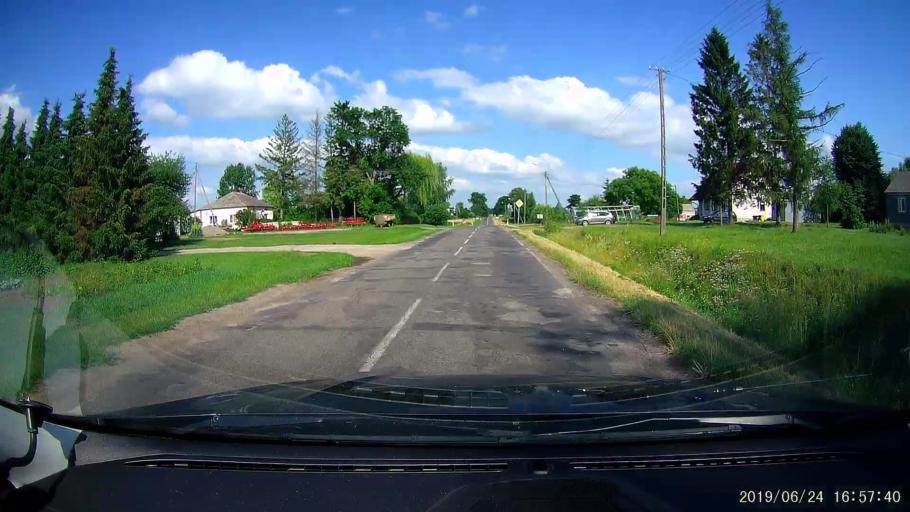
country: PL
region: Lublin Voivodeship
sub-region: Powiat tomaszowski
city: Telatyn
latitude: 50.5260
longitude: 23.8637
